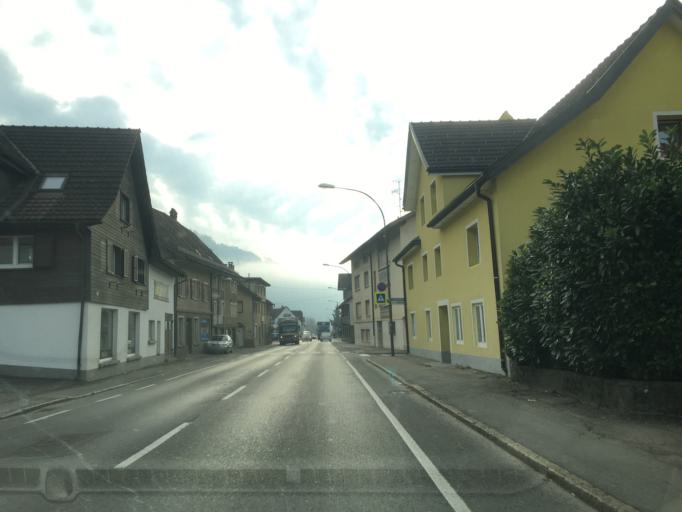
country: AT
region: Vorarlberg
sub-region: Politischer Bezirk Dornbirn
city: Hohenems
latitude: 47.3598
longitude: 9.6858
